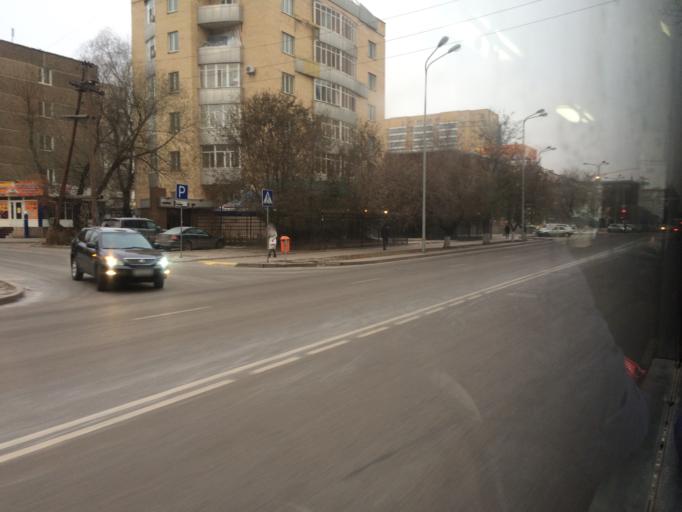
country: KZ
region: Astana Qalasy
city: Astana
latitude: 51.1688
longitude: 71.4395
